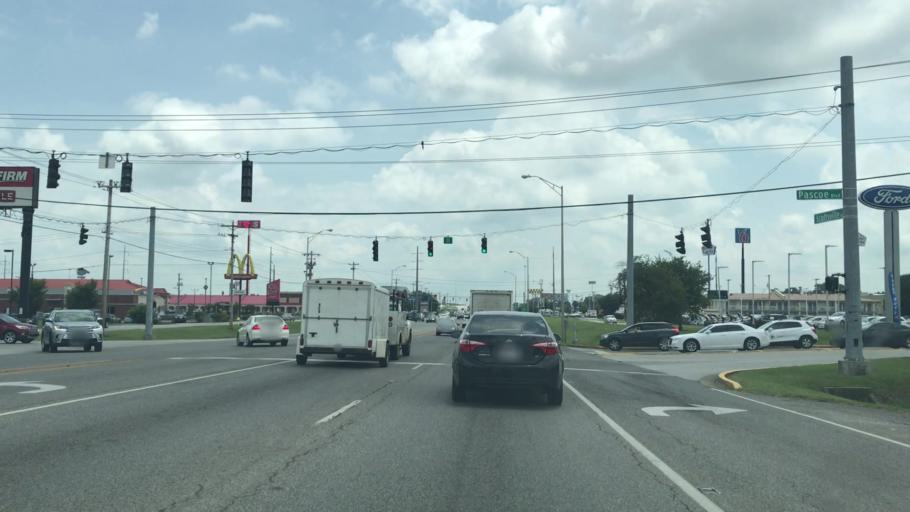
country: US
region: Kentucky
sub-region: Warren County
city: Bowling Green
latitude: 36.9432
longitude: -86.4222
